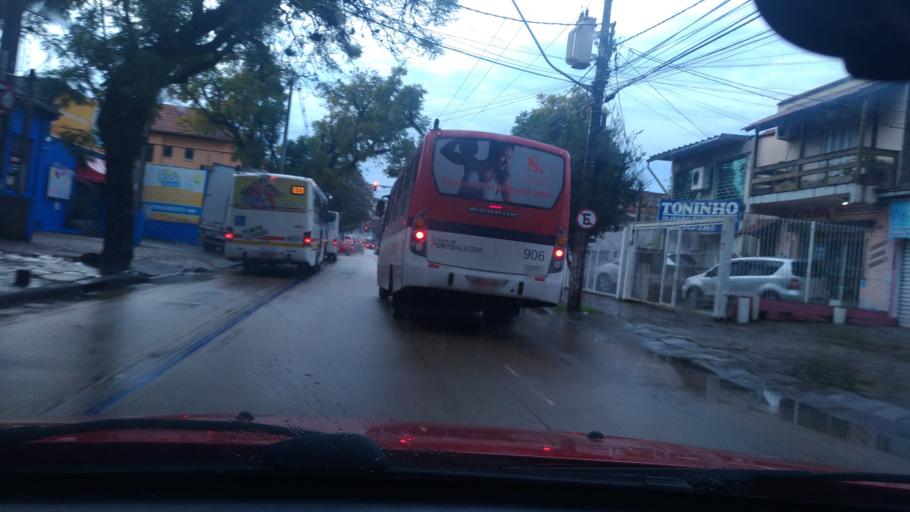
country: BR
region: Rio Grande do Sul
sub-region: Porto Alegre
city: Porto Alegre
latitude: -30.0072
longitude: -51.1945
